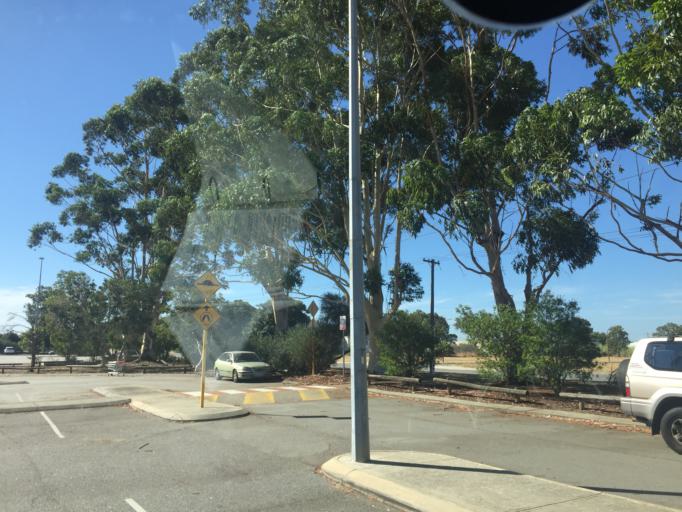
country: AU
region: Western Australia
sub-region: Gosnells
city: Maddington
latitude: -32.0519
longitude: 115.9788
